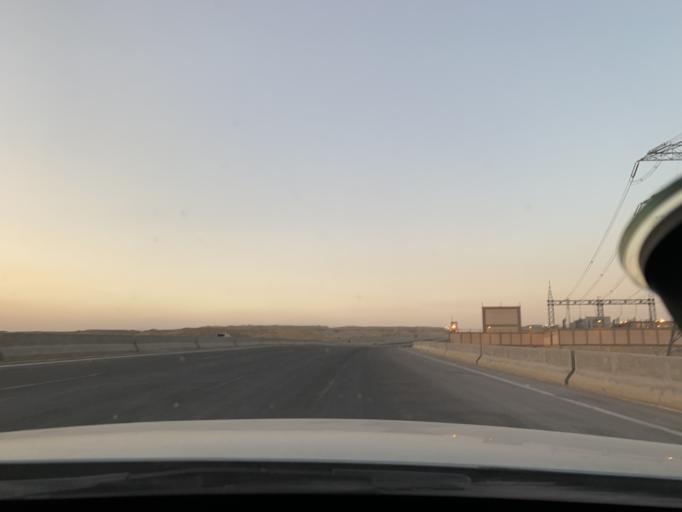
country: EG
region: Muhafazat al Qahirah
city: Halwan
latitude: 29.9366
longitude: 31.5290
